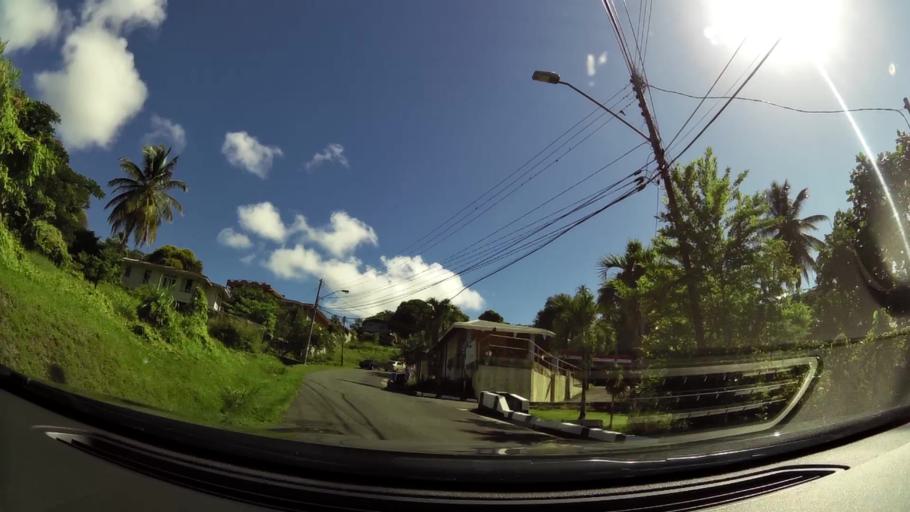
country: TT
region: Tobago
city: Scarborough
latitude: 11.1811
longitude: -60.7307
